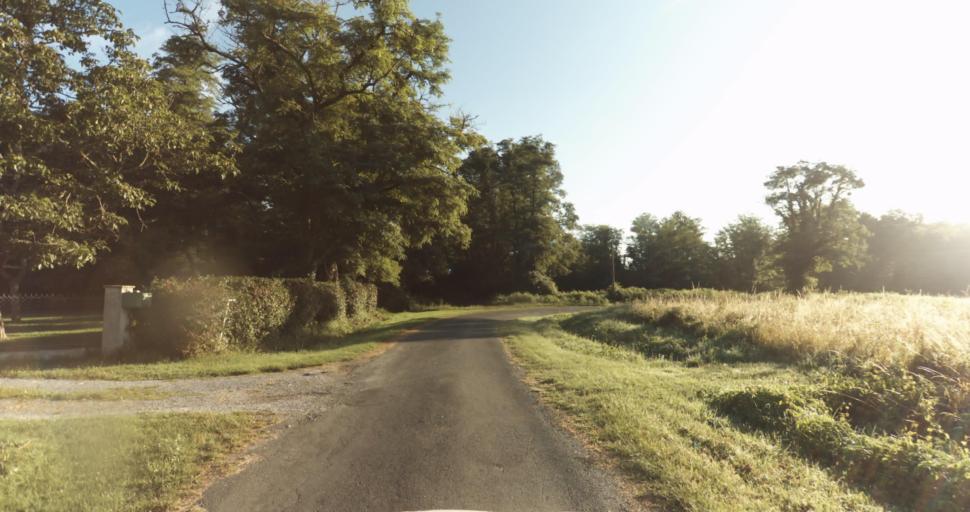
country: FR
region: Aquitaine
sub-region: Departement de la Gironde
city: Bazas
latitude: 44.4135
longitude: -0.2248
